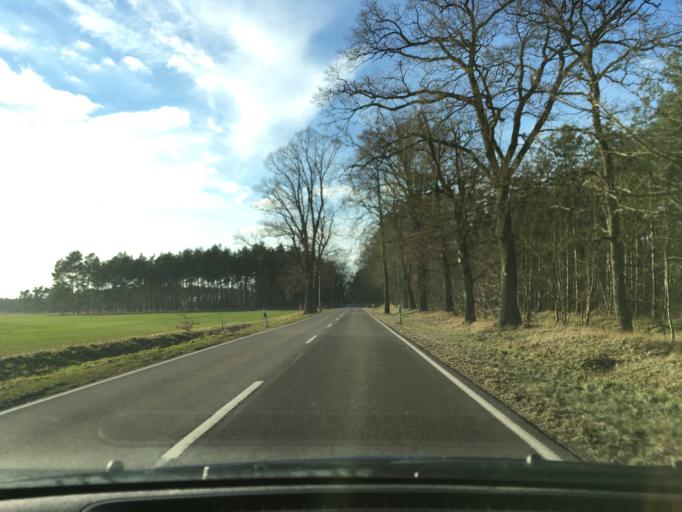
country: DE
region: Saxony-Anhalt
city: Luftkurort Arendsee
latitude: 52.8846
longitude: 11.5964
